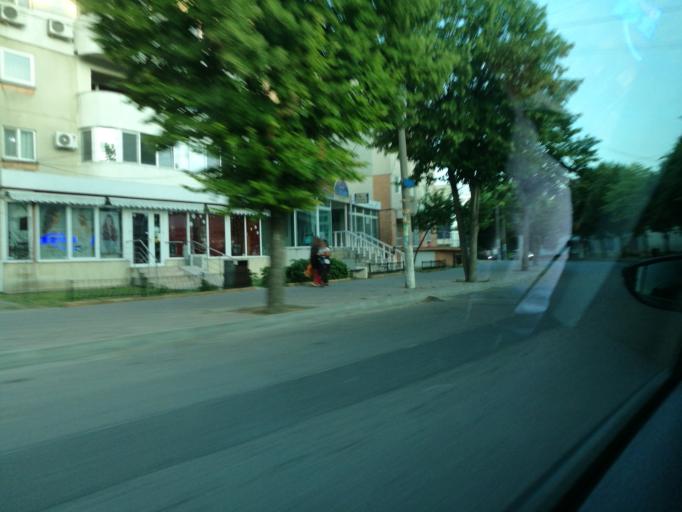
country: RO
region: Constanta
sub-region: Municipiul Mangalia
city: Mangalia
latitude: 43.8150
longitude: 28.5824
